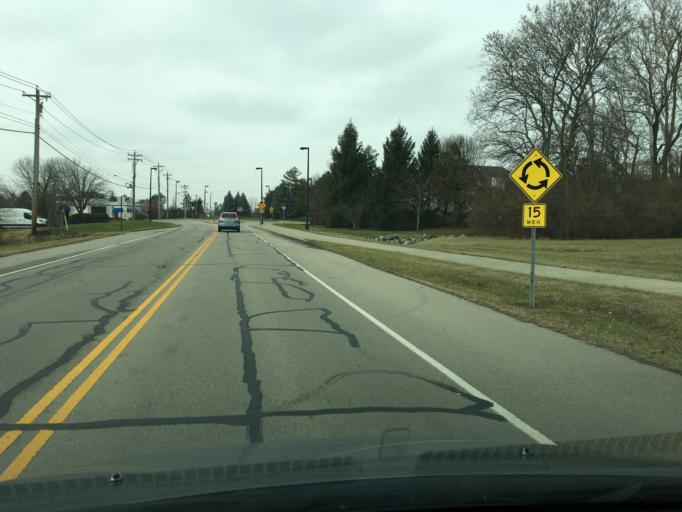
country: US
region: Ohio
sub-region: Butler County
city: Beckett Ridge
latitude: 39.3305
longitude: -84.4265
